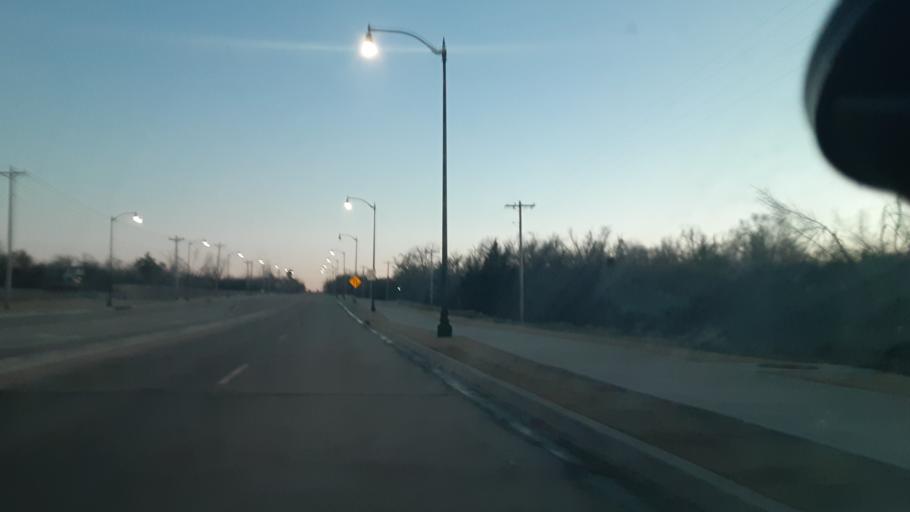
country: US
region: Oklahoma
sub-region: Oklahoma County
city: Edmond
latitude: 35.6813
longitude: -97.4251
